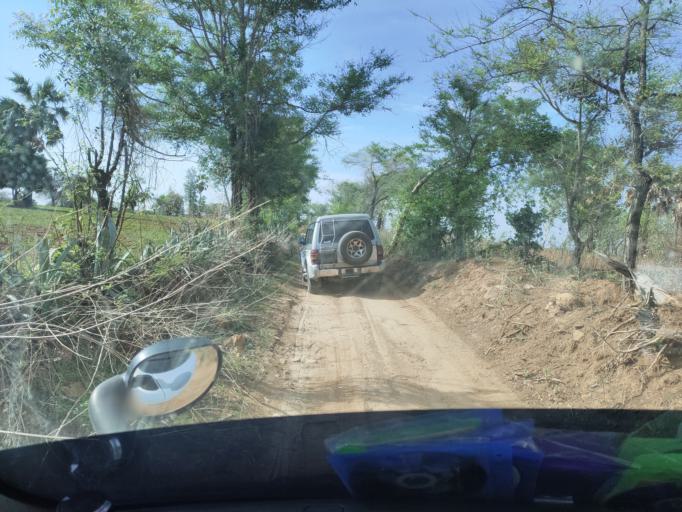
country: MM
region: Magway
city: Chauk
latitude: 20.9548
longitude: 94.9926
